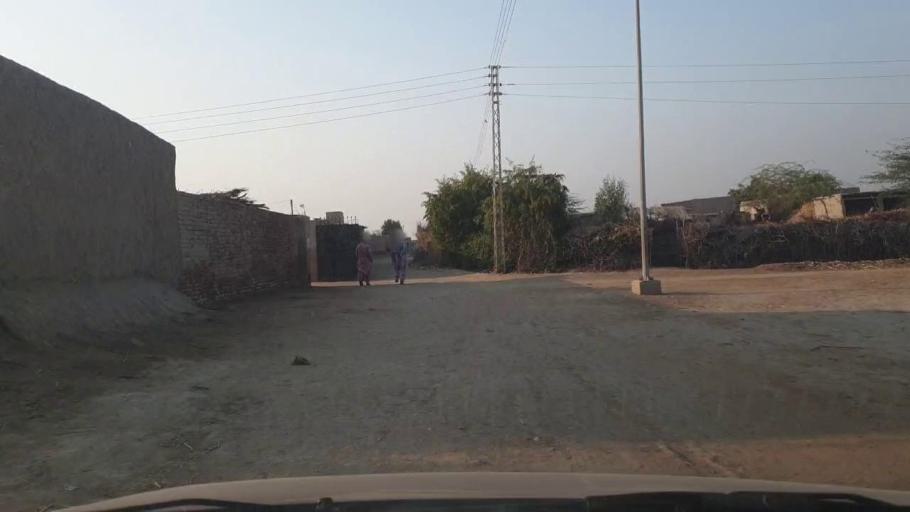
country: PK
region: Sindh
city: Mirwah Gorchani
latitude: 25.3729
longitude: 69.1245
